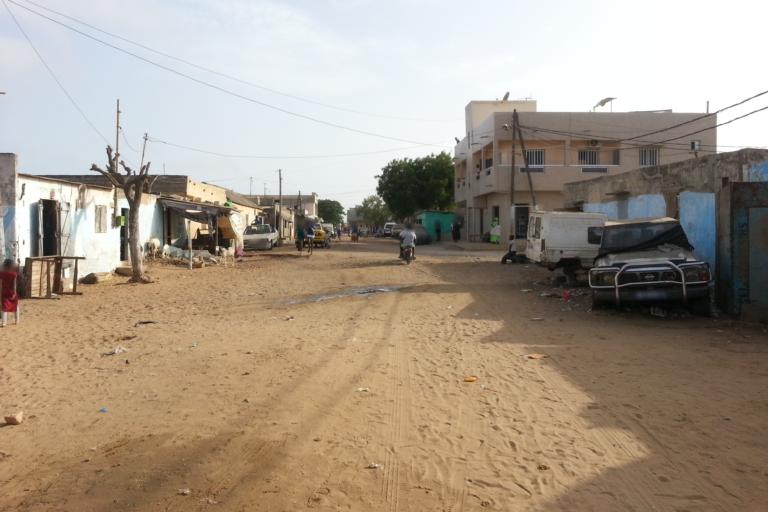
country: SN
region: Dakar
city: Pikine
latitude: 14.7665
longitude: -17.3860
